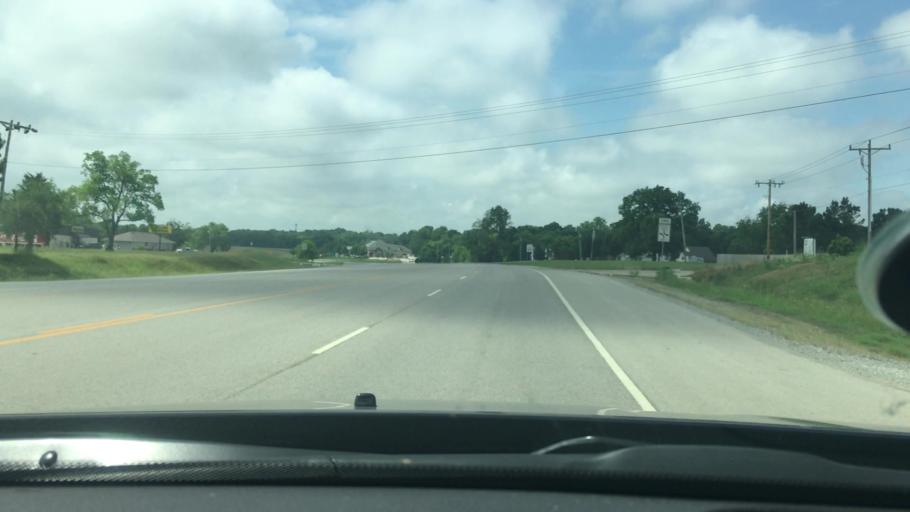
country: US
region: Oklahoma
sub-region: Bryan County
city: Durant
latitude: 34.0447
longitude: -96.3753
